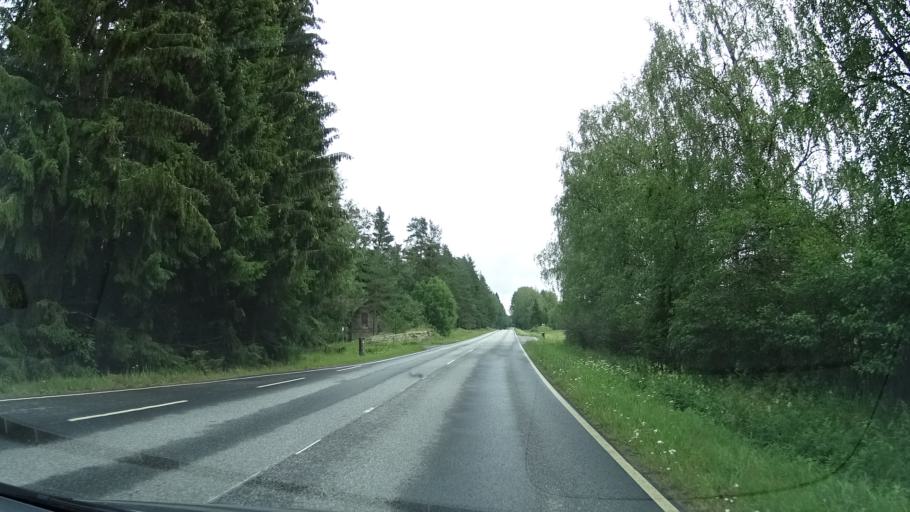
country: FI
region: Haeme
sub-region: Forssa
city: Humppila
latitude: 61.0981
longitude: 23.3271
